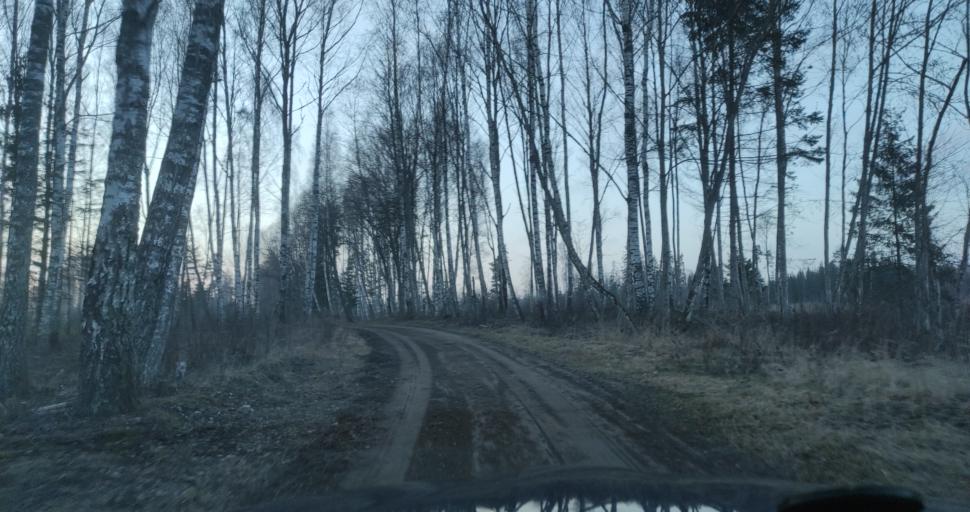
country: LV
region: Kuldigas Rajons
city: Kuldiga
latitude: 56.8117
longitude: 21.8264
